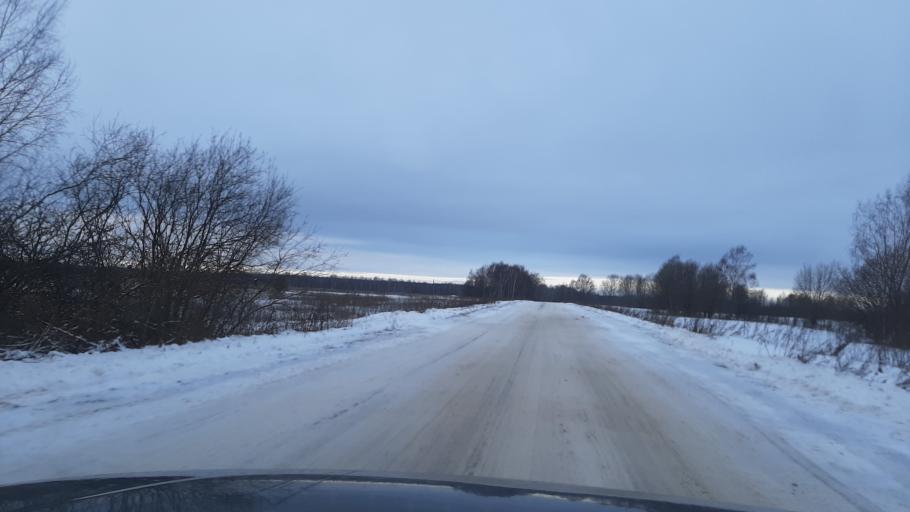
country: RU
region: Kostroma
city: Volgorechensk
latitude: 57.4364
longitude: 41.0567
